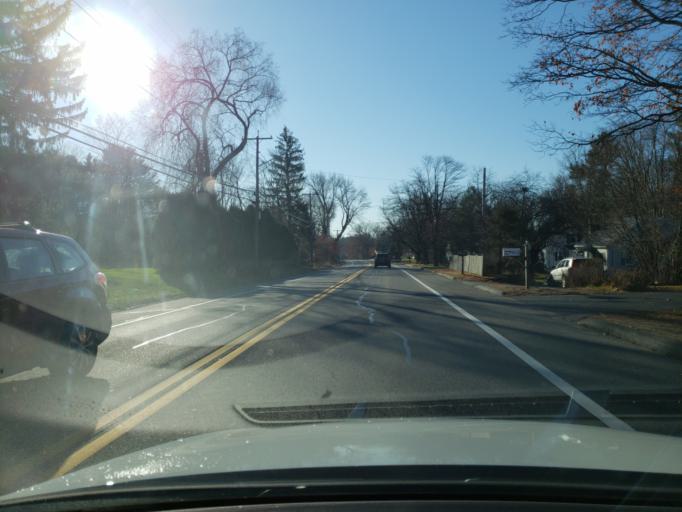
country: US
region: Massachusetts
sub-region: Essex County
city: Andover
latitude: 42.6208
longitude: -71.1257
